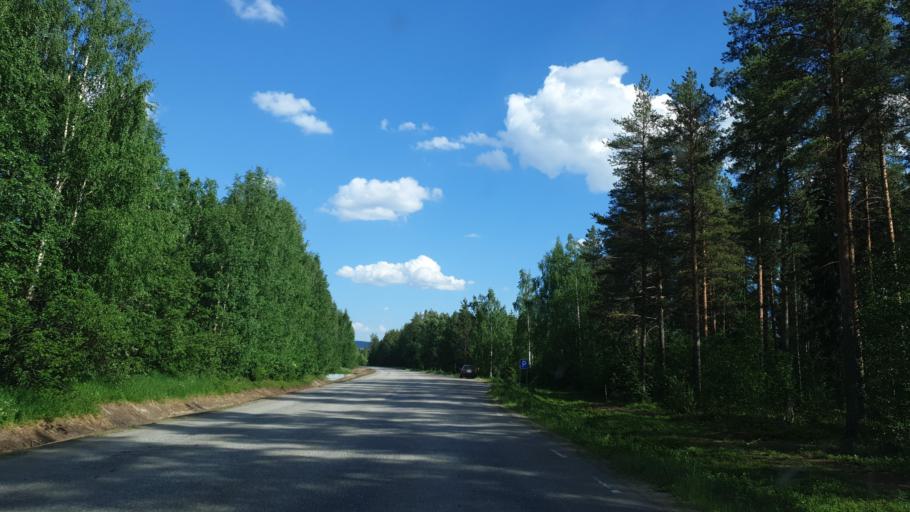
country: SE
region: Norrbotten
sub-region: Alvsbyns Kommun
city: AElvsbyn
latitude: 65.8358
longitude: 20.5210
